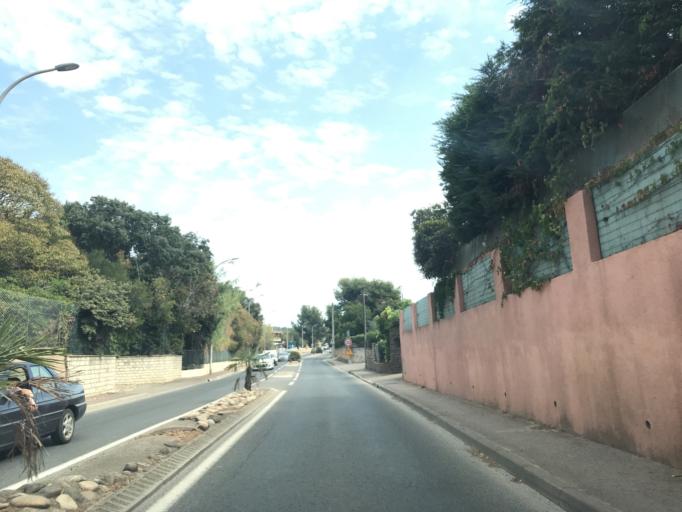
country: FR
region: Provence-Alpes-Cote d'Azur
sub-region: Departement du Var
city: Six-Fours-les-Plages
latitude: 43.0884
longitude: 5.8281
